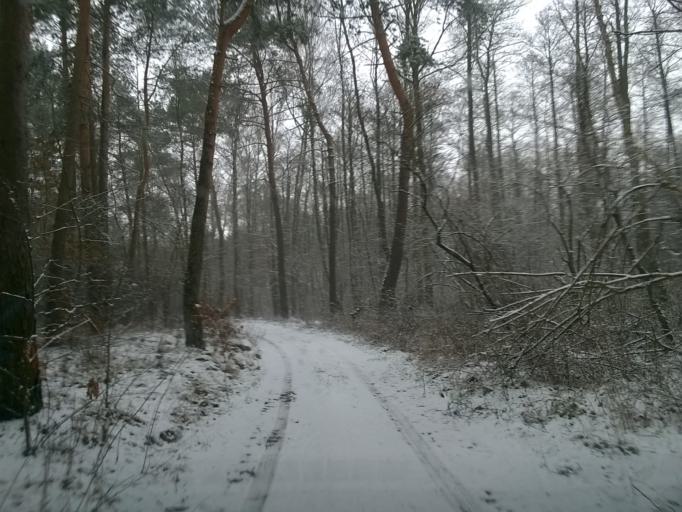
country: PL
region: Kujawsko-Pomorskie
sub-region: Powiat swiecki
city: Swiecie
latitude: 53.4217
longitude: 18.3882
